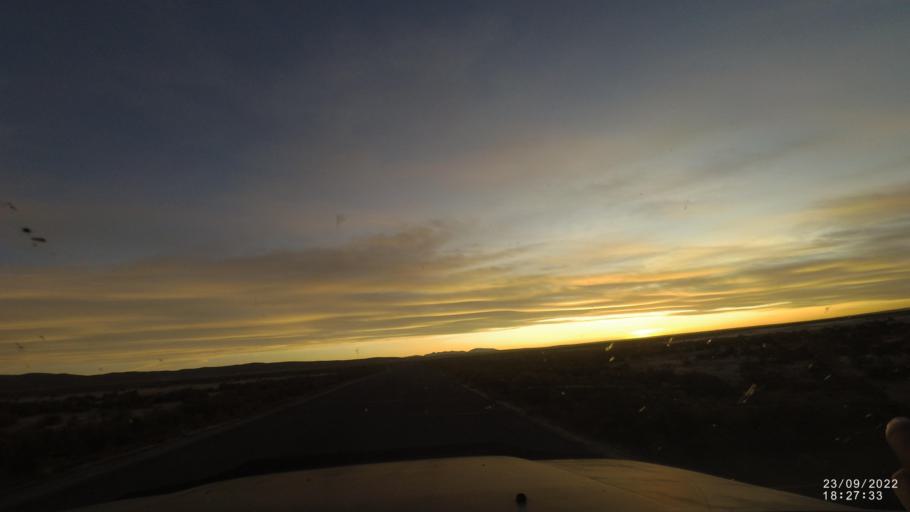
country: BO
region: Oruro
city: Challapata
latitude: -19.3292
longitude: -67.1690
